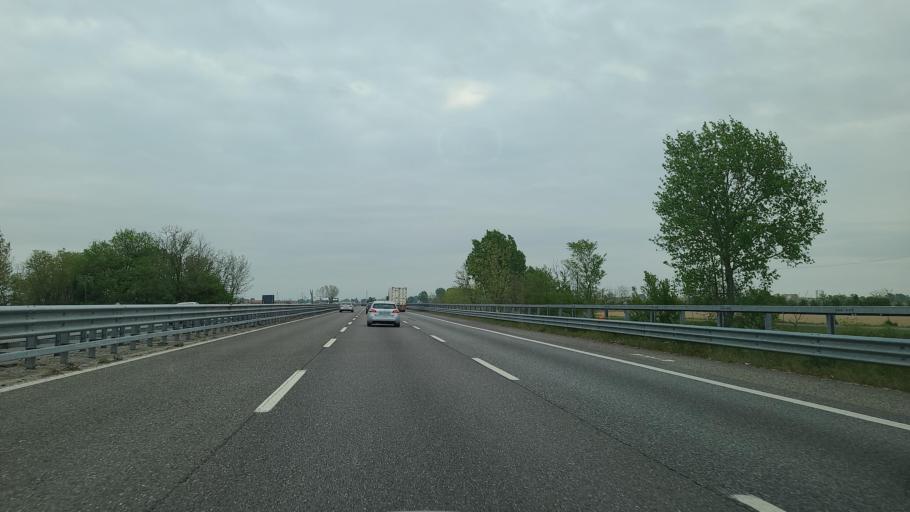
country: IT
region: Lombardy
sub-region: Citta metropolitana di Milano
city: Vernate
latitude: 45.3052
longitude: 9.0727
